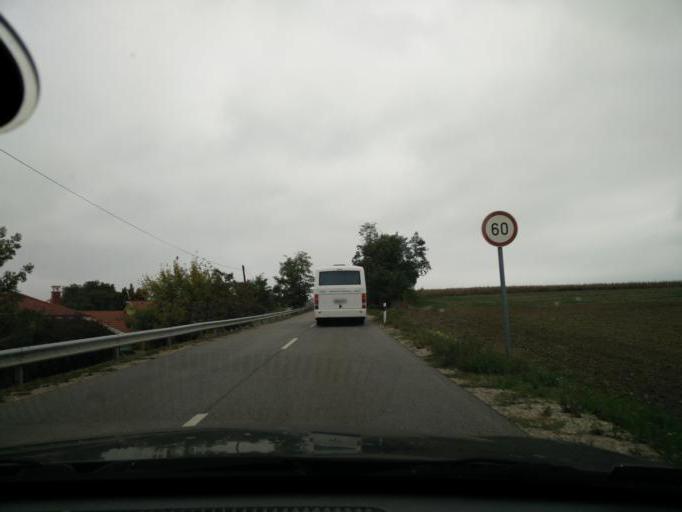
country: HU
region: Komarom-Esztergom
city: Bajna
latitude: 47.6840
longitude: 18.6106
